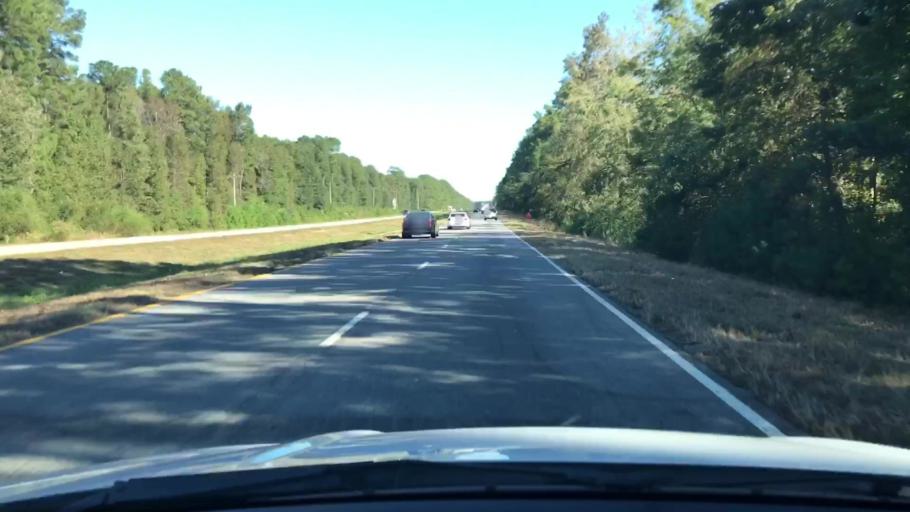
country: US
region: South Carolina
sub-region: Charleston County
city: Ravenel
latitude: 32.7825
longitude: -80.2008
